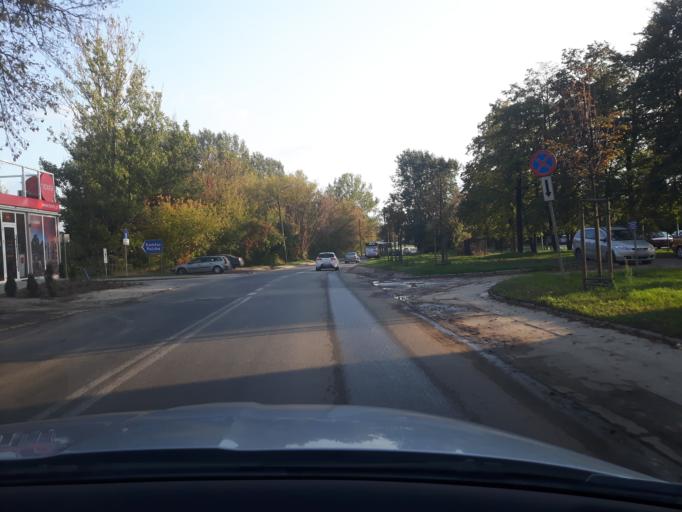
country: PL
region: Masovian Voivodeship
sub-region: Warszawa
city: Wlochy
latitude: 52.1595
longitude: 20.9924
